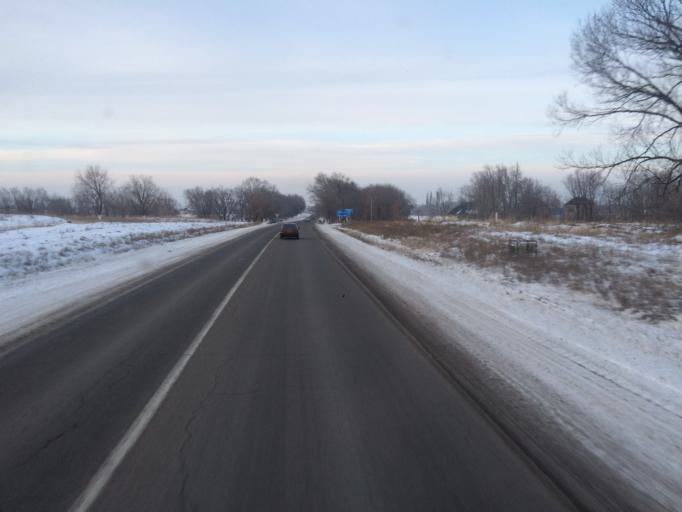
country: KZ
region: Almaty Oblysy
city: Burunday
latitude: 43.3252
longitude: 76.6628
